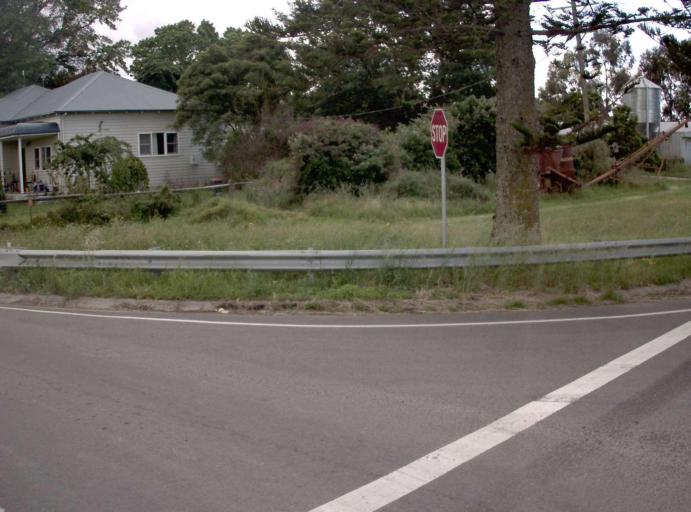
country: AU
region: Victoria
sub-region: Baw Baw
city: Warragul
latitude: -38.1001
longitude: 145.9220
